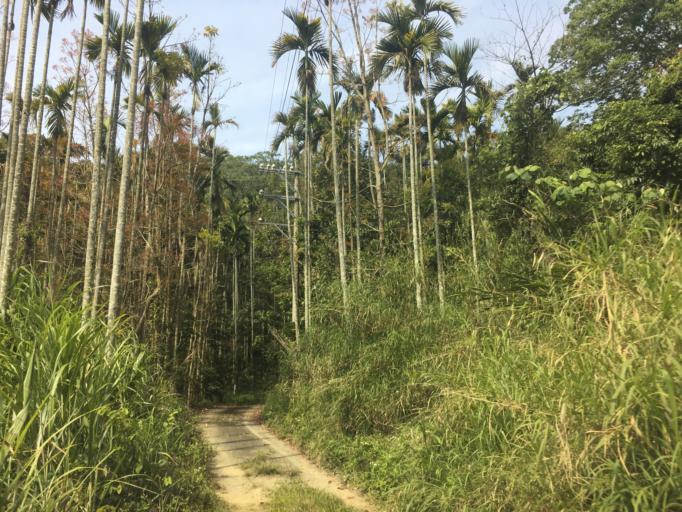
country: TW
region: Taiwan
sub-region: Taichung City
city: Taichung
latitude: 24.1342
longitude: 120.8246
